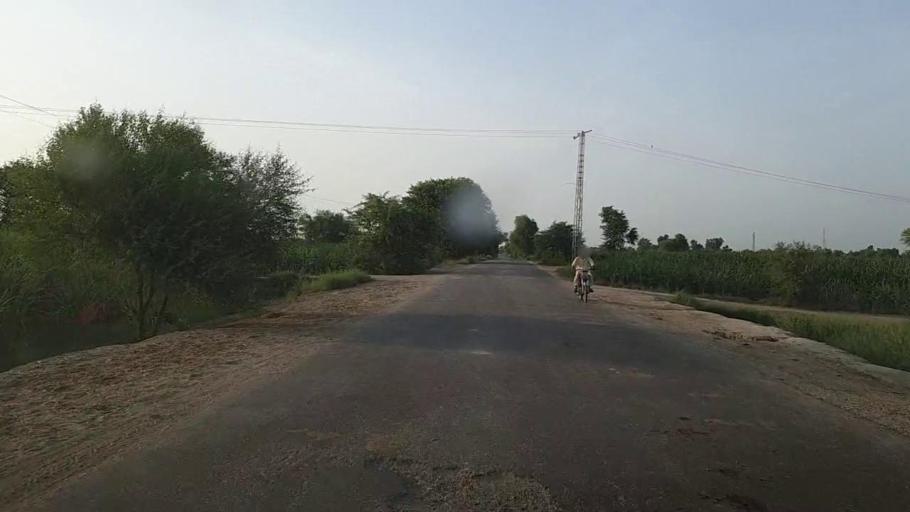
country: PK
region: Sindh
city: Ubauro
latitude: 28.1809
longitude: 69.8286
